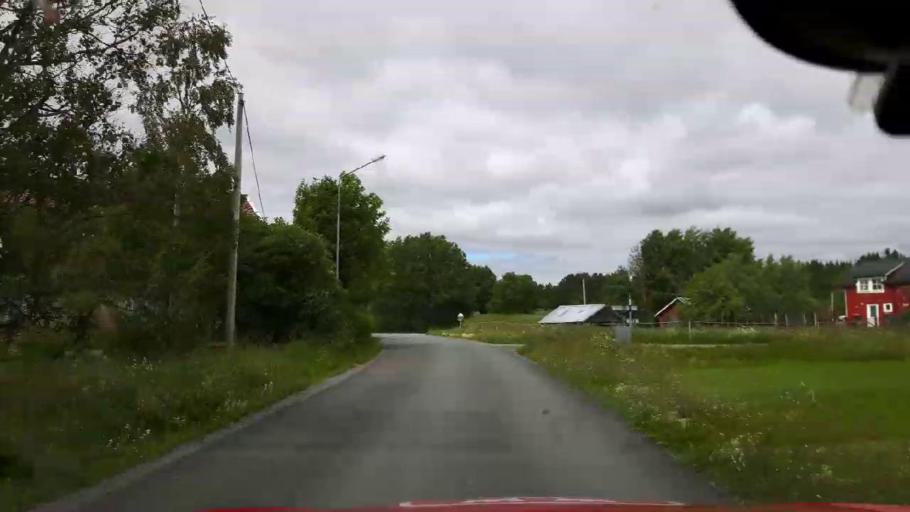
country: SE
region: Jaemtland
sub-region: OEstersunds Kommun
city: Brunflo
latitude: 63.0747
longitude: 14.8856
